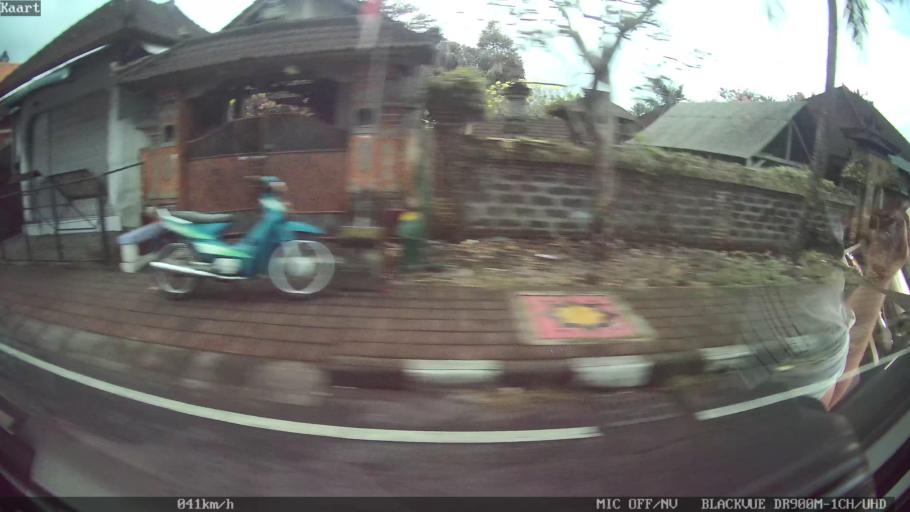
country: ID
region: Bali
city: Banjar Cemenggon
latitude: -8.5348
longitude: 115.1999
